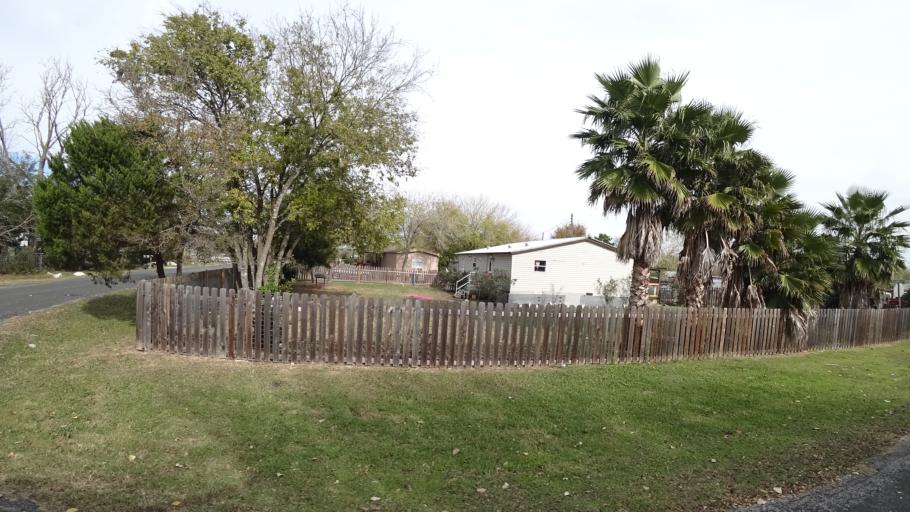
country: US
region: Texas
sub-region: Travis County
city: Garfield
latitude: 30.1306
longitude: -97.6185
